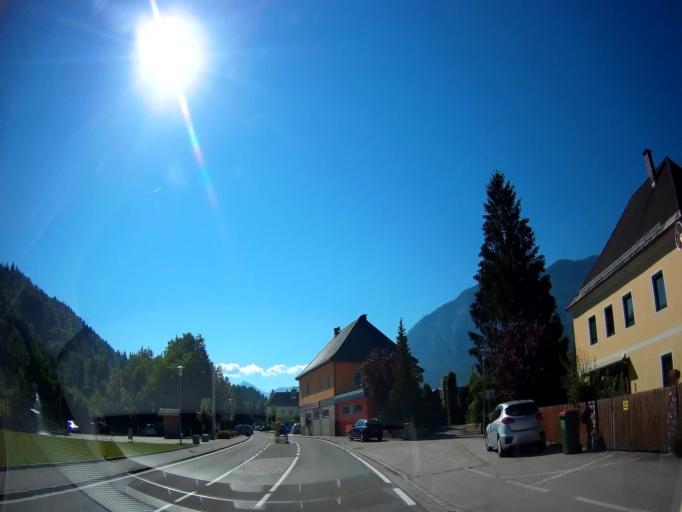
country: AT
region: Carinthia
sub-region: Politischer Bezirk Volkermarkt
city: Gallizien
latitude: 46.5592
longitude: 14.5073
